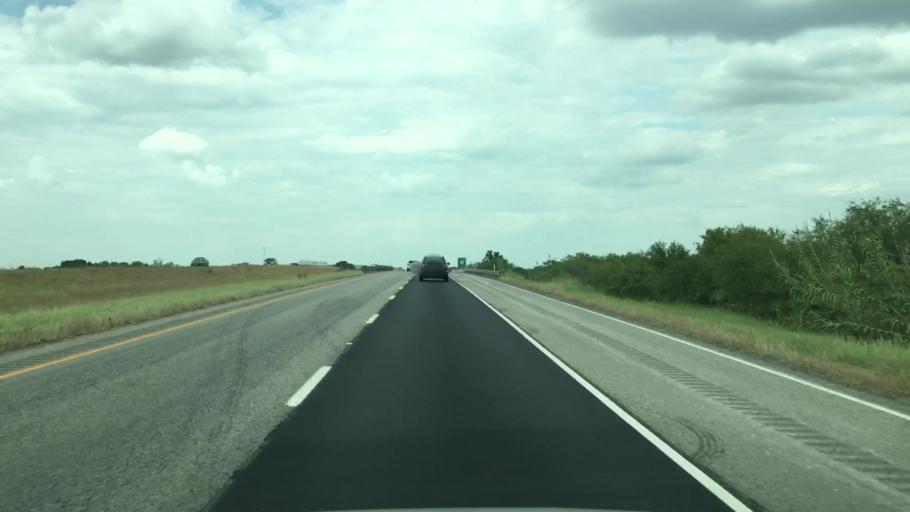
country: US
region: Texas
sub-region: Atascosa County
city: Pleasanton
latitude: 29.0851
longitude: -98.4328
